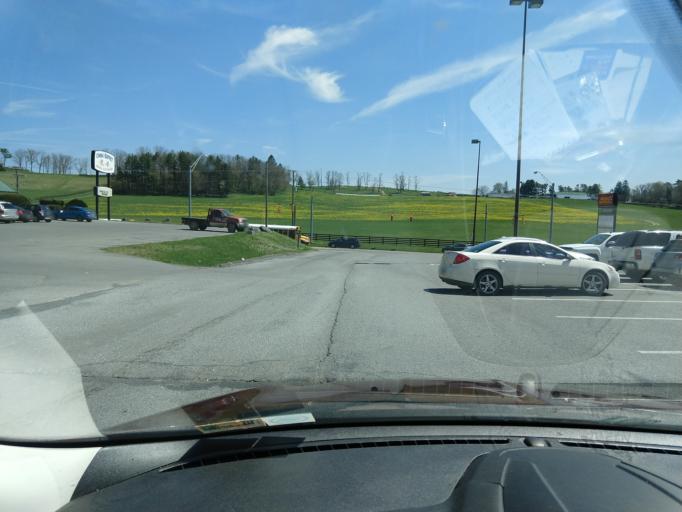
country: US
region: West Virginia
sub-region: Greenbrier County
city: Fairlea
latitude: 37.7896
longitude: -80.4512
